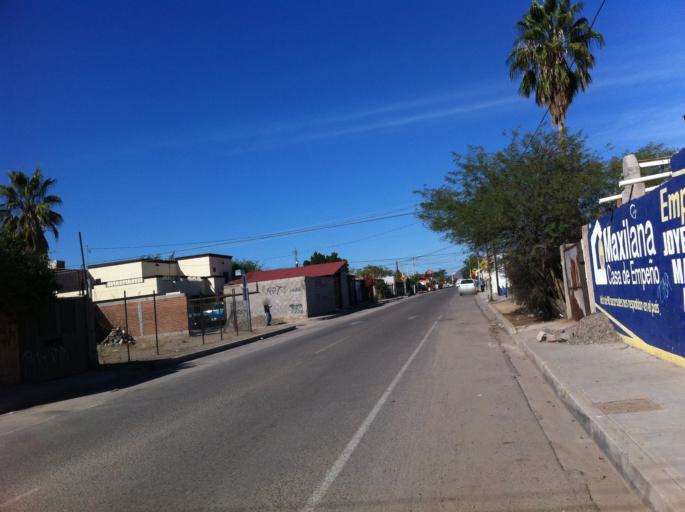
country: MX
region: Sonora
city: Hermosillo
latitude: 29.1056
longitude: -111.0113
